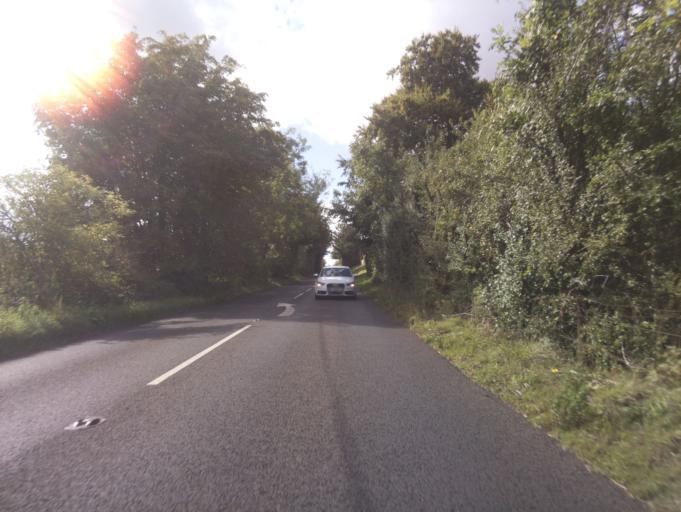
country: GB
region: England
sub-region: Wiltshire
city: Allington
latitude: 51.1173
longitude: -1.6362
